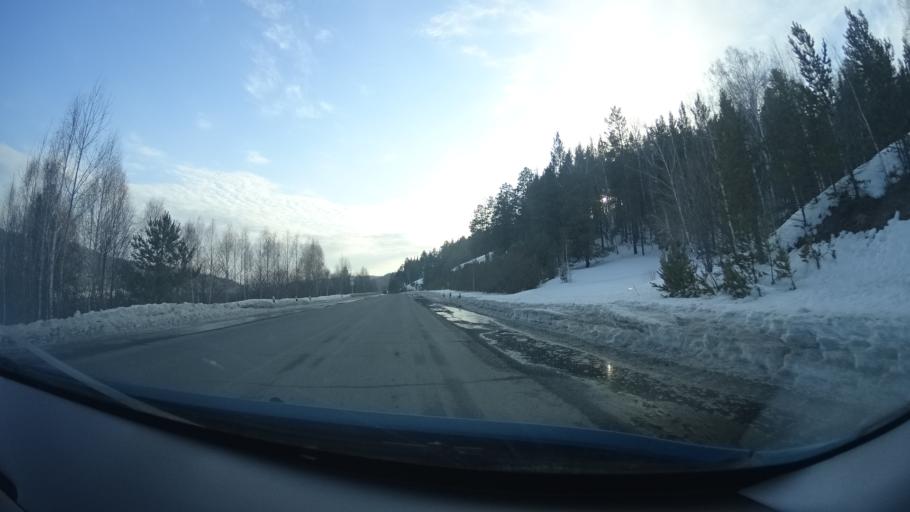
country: RU
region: Bashkortostan
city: Abzakovo
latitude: 53.4579
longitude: 58.3218
